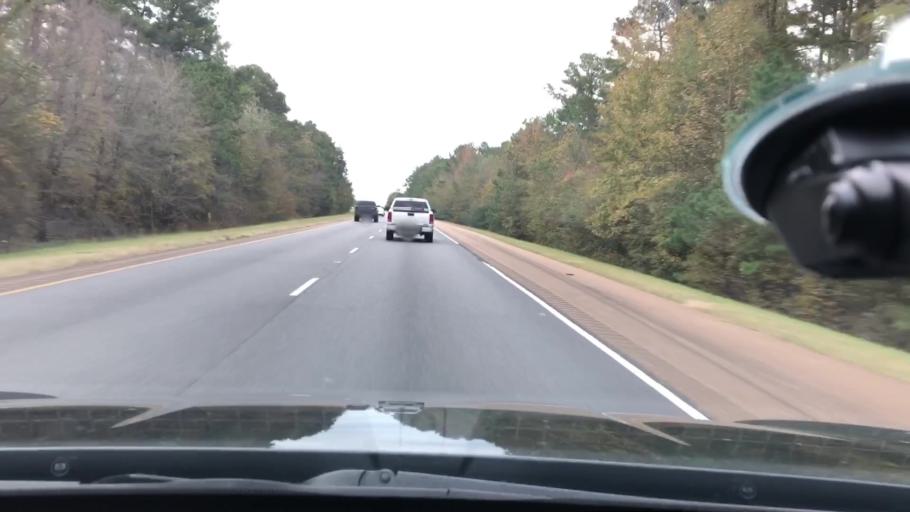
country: US
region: Arkansas
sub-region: Nevada County
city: Prescott
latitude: 33.8742
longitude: -93.3360
